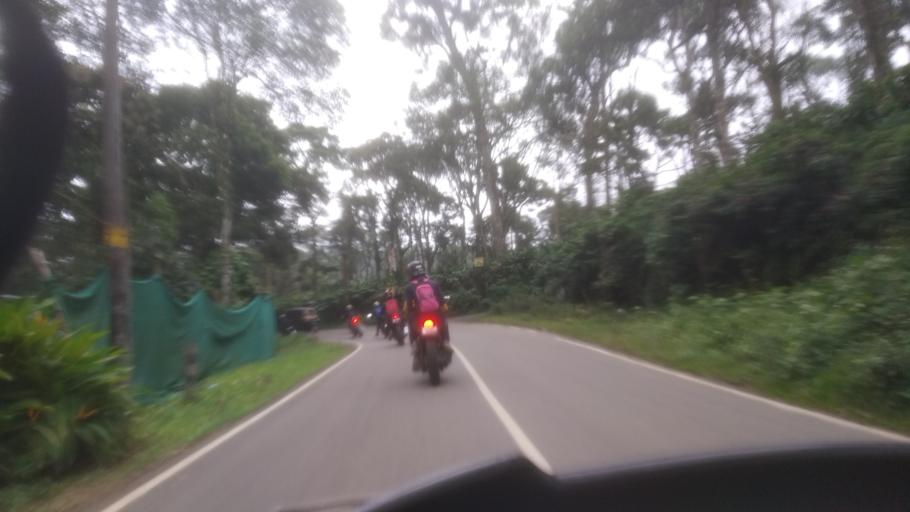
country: IN
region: Tamil Nadu
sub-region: Theni
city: Kombai
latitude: 9.8958
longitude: 77.1951
